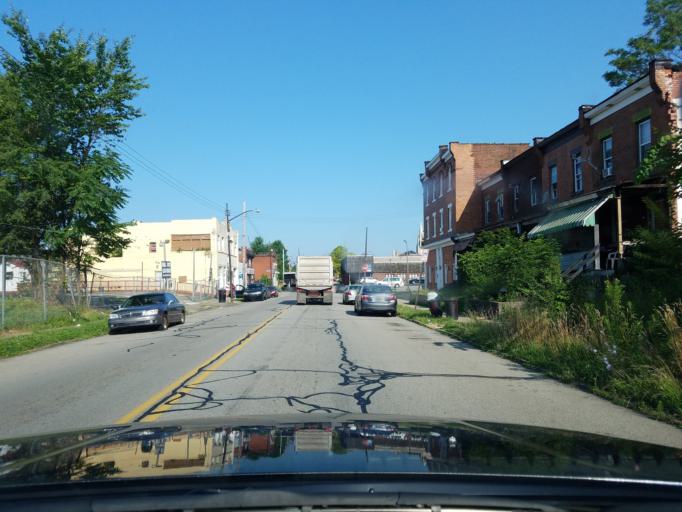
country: US
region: Pennsylvania
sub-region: Allegheny County
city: Wilkinsburg
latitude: 40.4540
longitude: -79.8945
